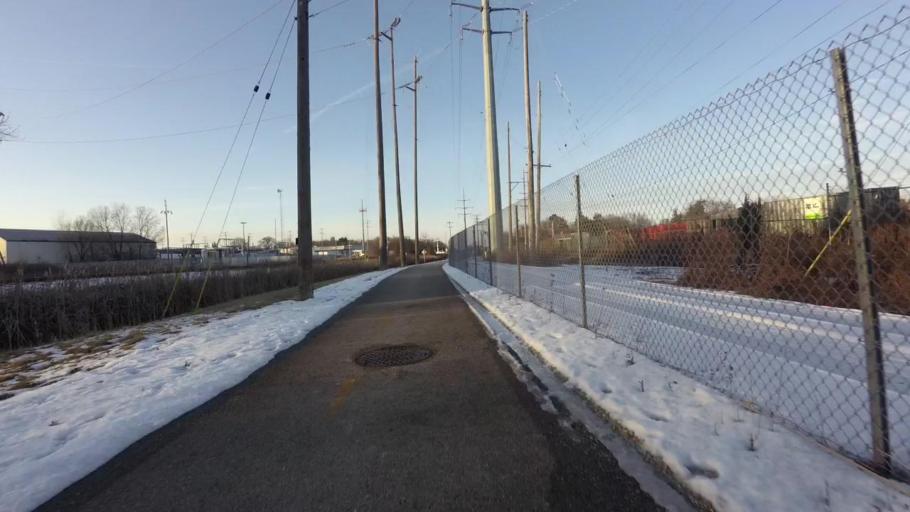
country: US
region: Wisconsin
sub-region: Milwaukee County
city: Glendale
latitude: 43.1323
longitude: -87.9476
